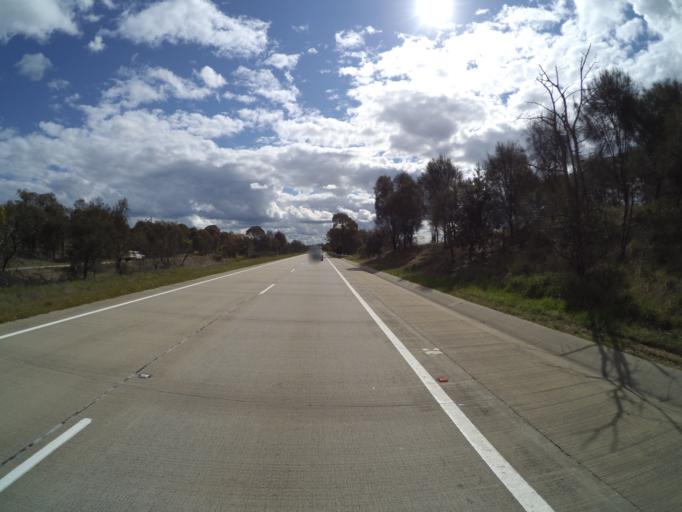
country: AU
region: New South Wales
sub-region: Yass Valley
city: Gundaroo
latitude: -34.7886
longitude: 149.2103
